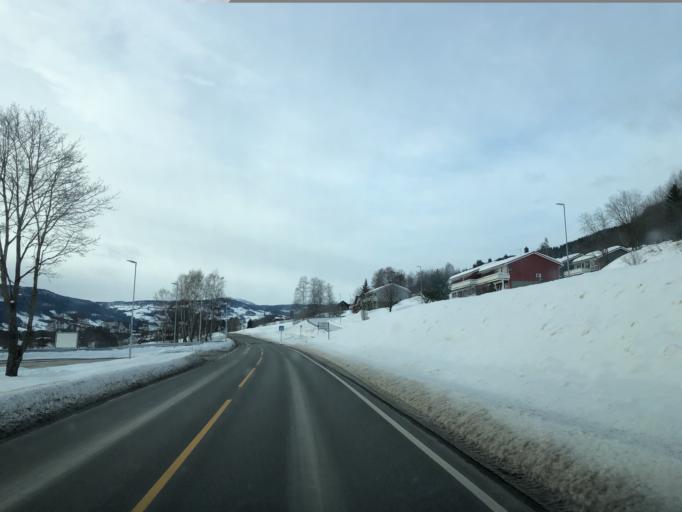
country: NO
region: Oppland
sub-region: Gausdal
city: Segalstad bru
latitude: 61.2341
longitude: 10.2107
